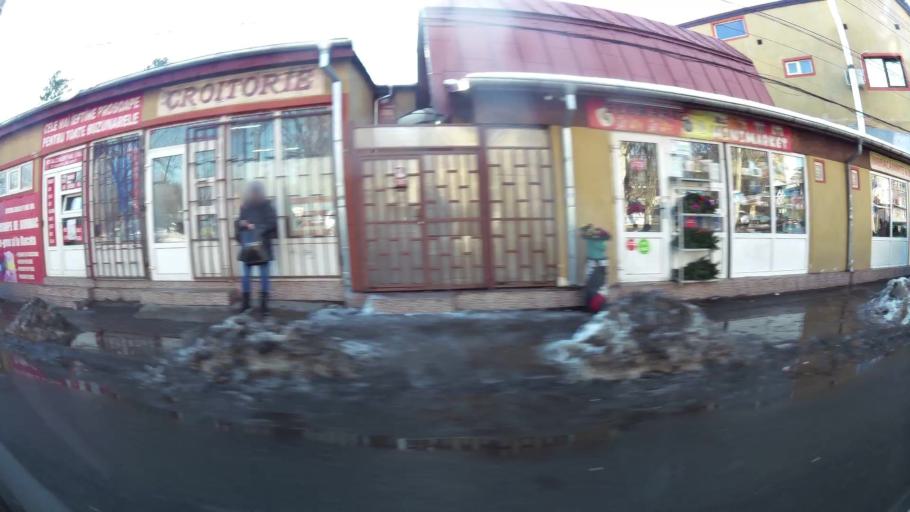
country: RO
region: Bucuresti
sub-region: Municipiul Bucuresti
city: Bucuresti
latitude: 44.3837
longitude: 26.0815
